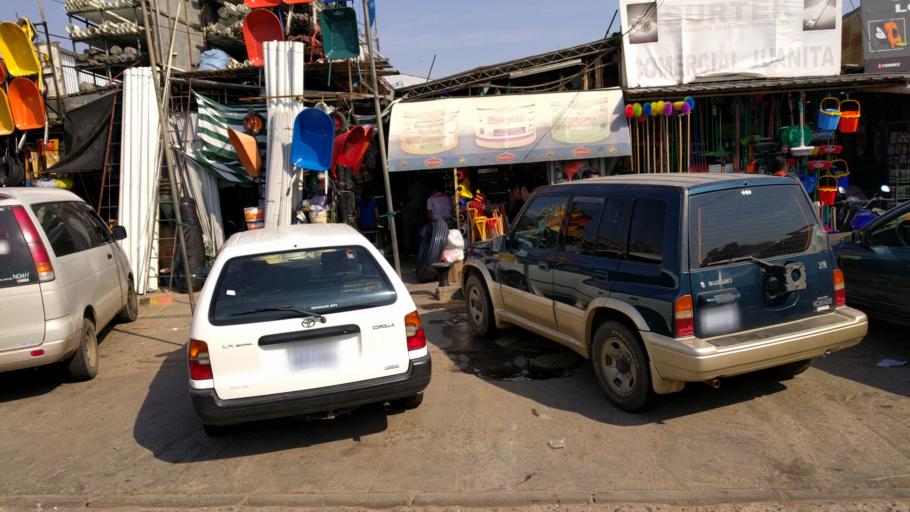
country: BO
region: Santa Cruz
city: Santa Cruz de la Sierra
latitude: -17.7851
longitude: -63.1587
